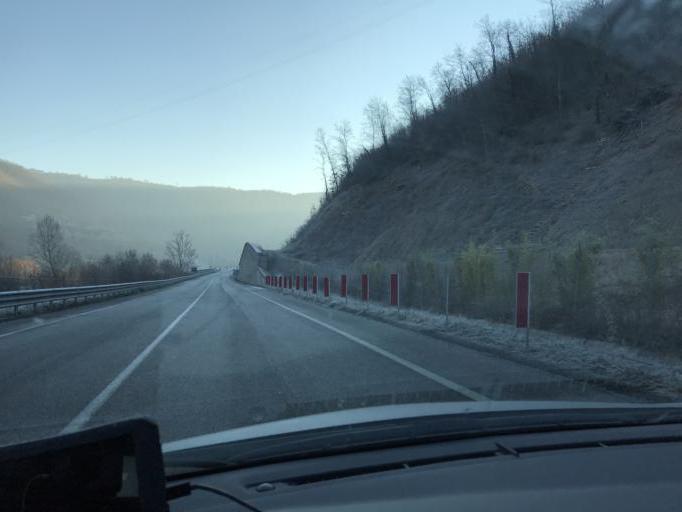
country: IT
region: Latium
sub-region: Provincia di Rieti
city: Cittaducale
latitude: 42.3527
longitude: 12.9507
